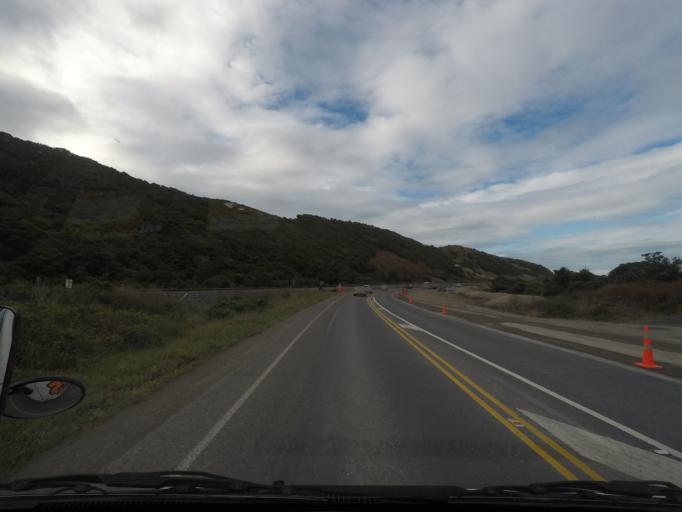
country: NZ
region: Canterbury
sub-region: Kaikoura District
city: Kaikoura
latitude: -42.2167
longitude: 173.8608
